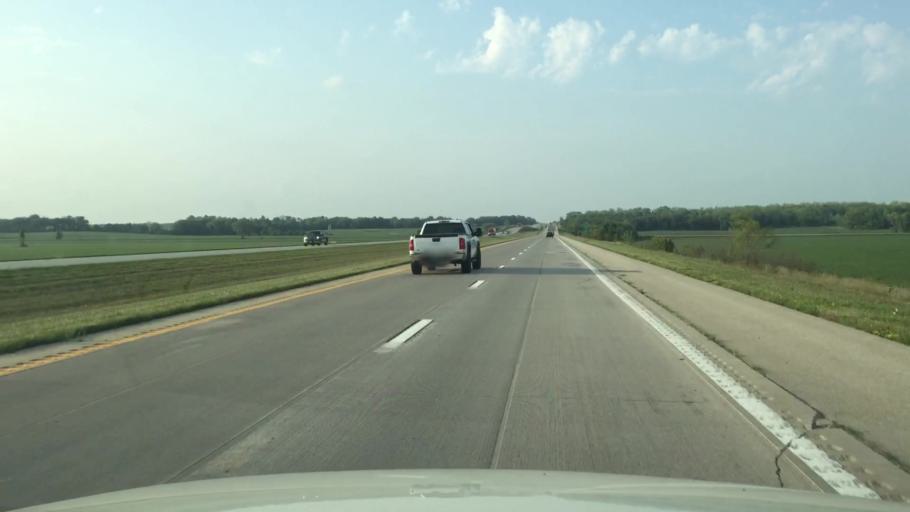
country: US
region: Missouri
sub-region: Daviess County
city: Gallatin
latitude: 40.0401
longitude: -94.0948
